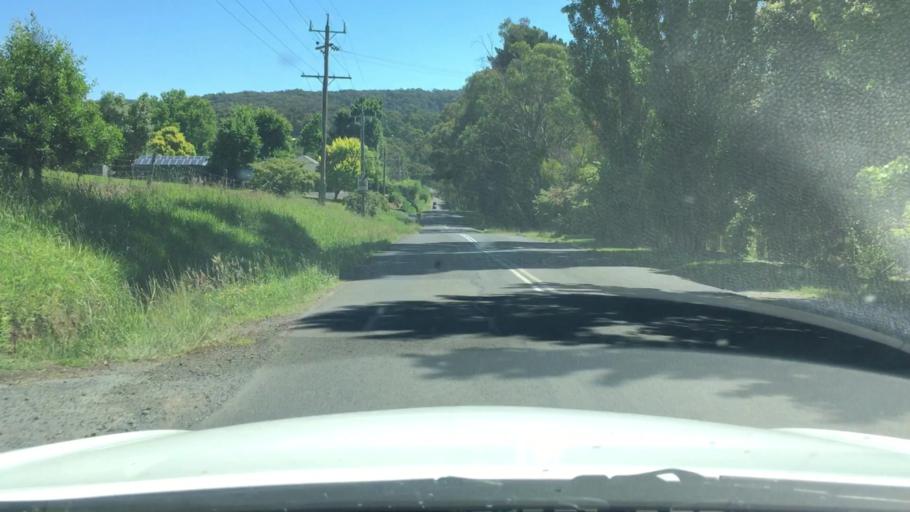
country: AU
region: Victoria
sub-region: Yarra Ranges
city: Mount Evelyn
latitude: -37.8027
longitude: 145.4144
